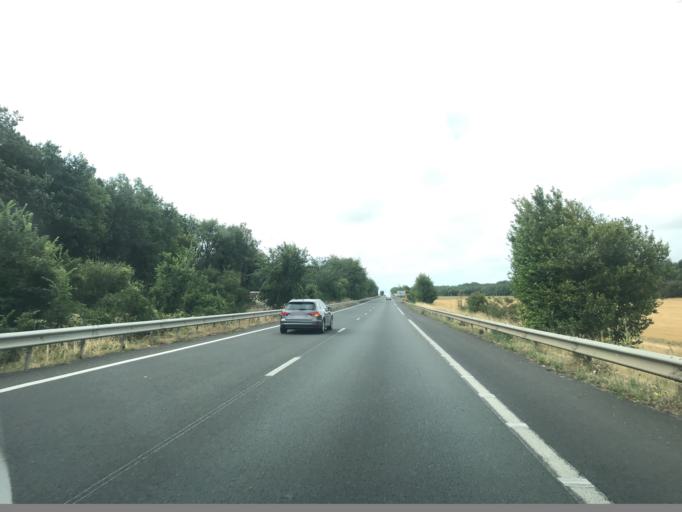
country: FR
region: Poitou-Charentes
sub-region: Departement de la Vienne
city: Celle-Levescault
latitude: 46.3889
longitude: 0.2224
